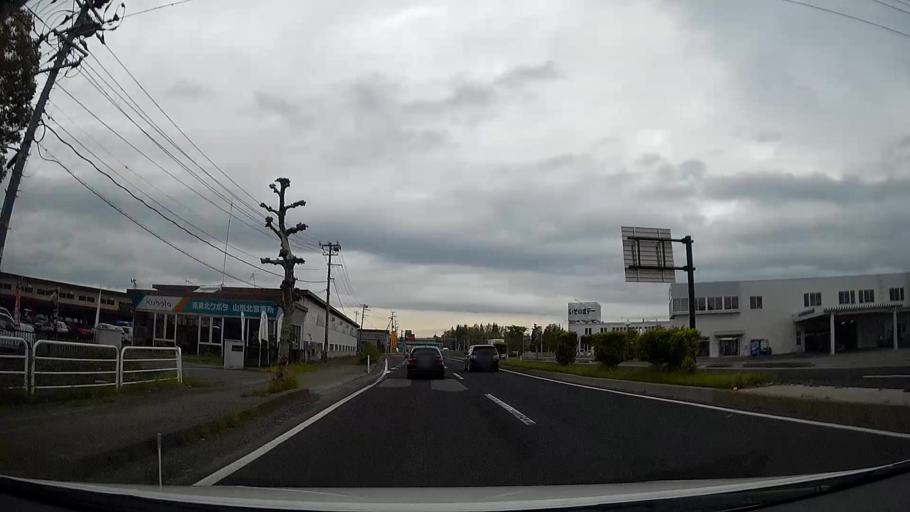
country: JP
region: Yamagata
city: Yamagata-shi
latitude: 38.2875
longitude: 140.3612
